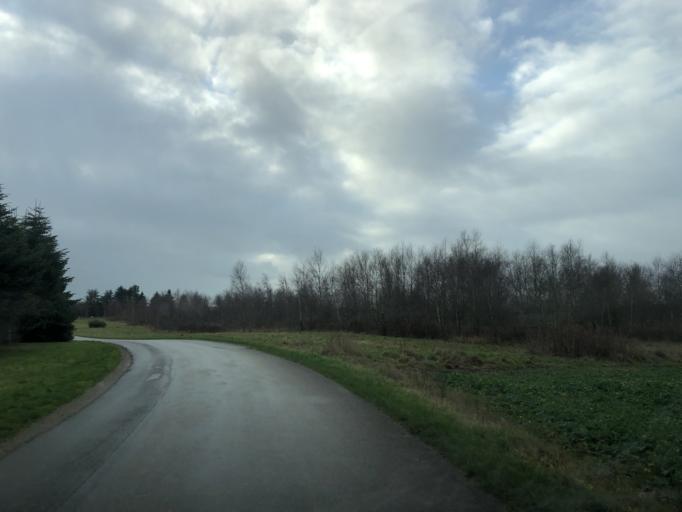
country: DK
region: North Denmark
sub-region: Rebild Kommune
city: Stovring
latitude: 56.9161
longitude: 9.7992
